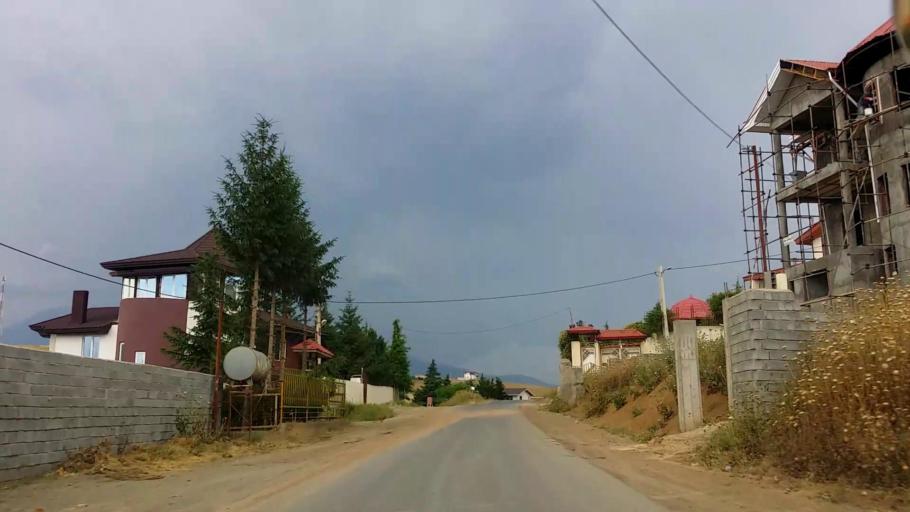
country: IR
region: Mazandaran
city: Chalus
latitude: 36.5155
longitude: 51.2493
